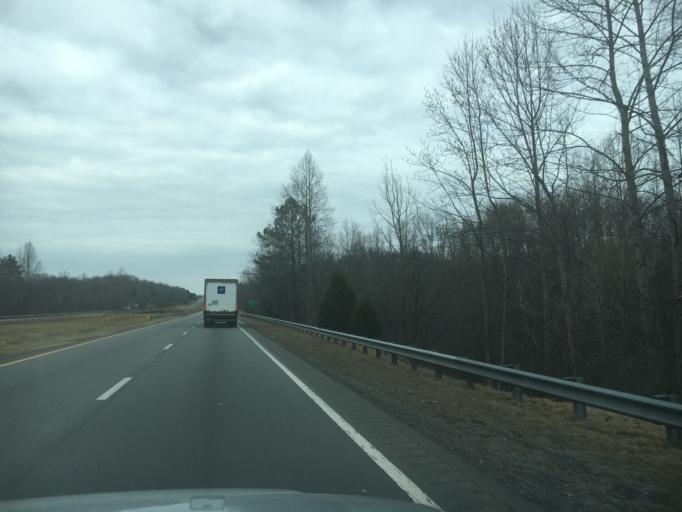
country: US
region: North Carolina
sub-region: Gaston County
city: Dallas
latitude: 35.3978
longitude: -81.2093
